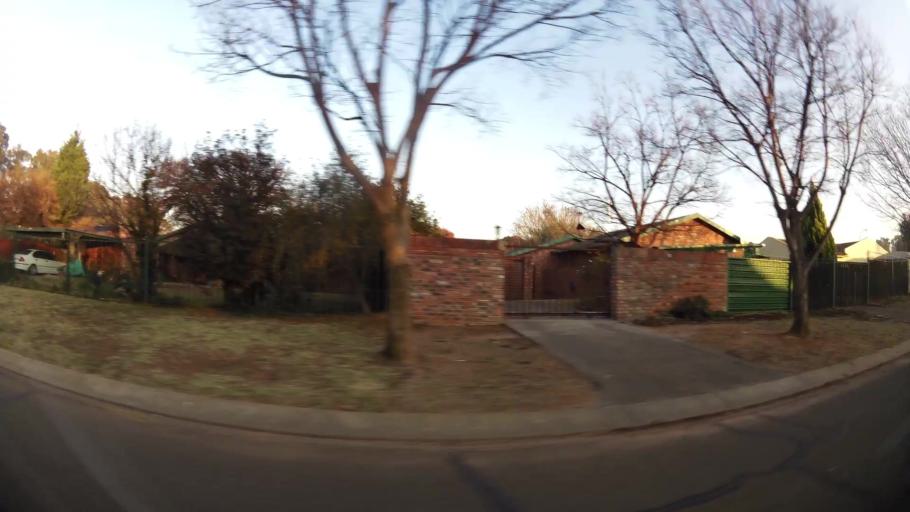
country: ZA
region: Orange Free State
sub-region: Mangaung Metropolitan Municipality
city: Bloemfontein
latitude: -29.1064
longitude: 26.1490
